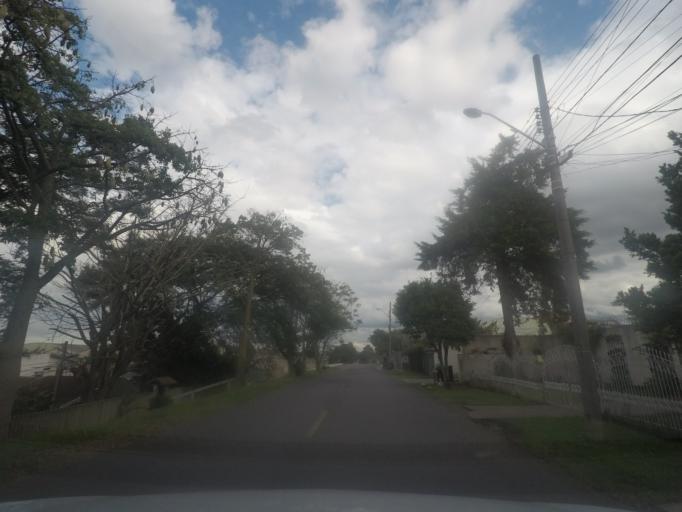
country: BR
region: Parana
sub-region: Pinhais
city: Pinhais
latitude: -25.4623
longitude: -49.2200
